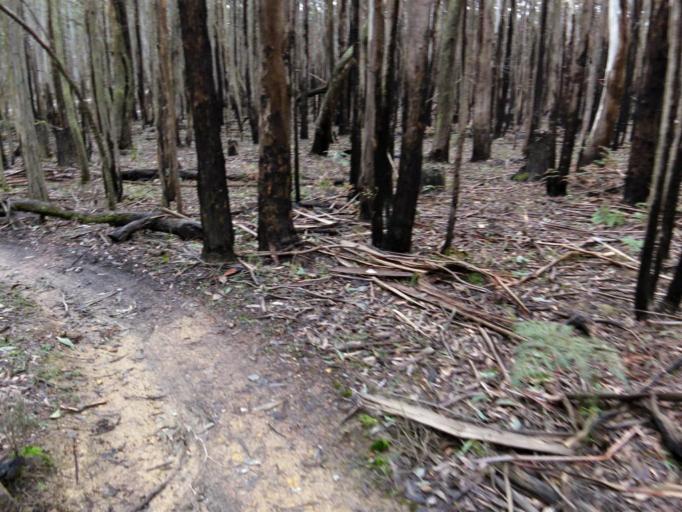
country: AU
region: Victoria
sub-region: Moorabool
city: Bacchus Marsh
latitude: -37.4232
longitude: 144.4887
